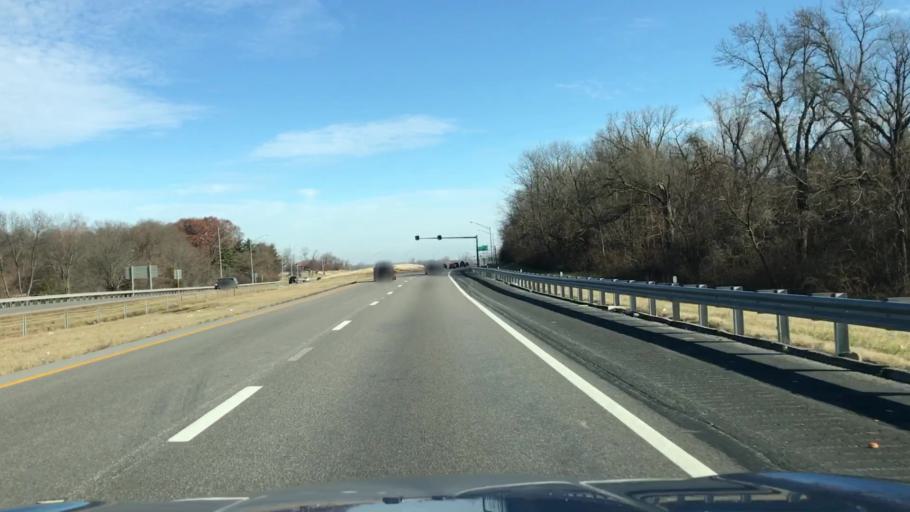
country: US
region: Missouri
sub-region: Saint Louis County
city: Glasgow Village
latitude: 38.7676
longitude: -90.1907
